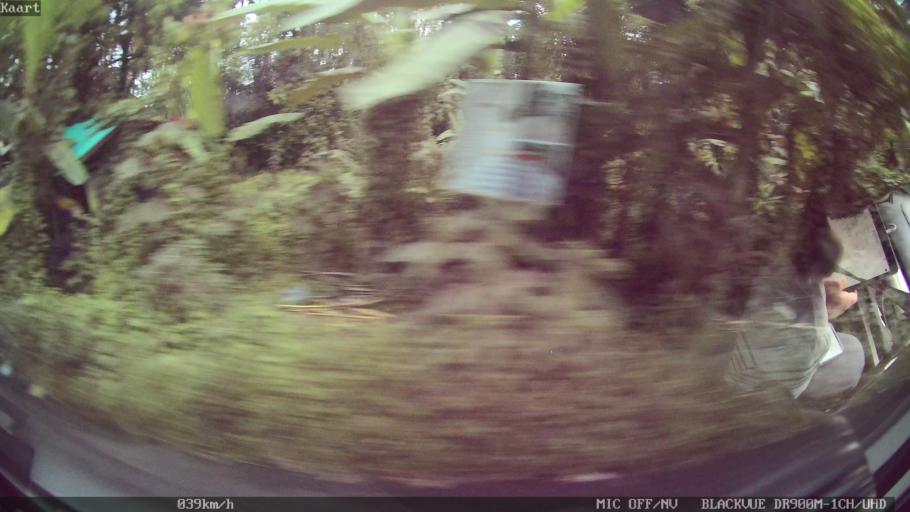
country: ID
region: Bali
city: Banjar Parekan
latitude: -8.5717
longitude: 115.2098
